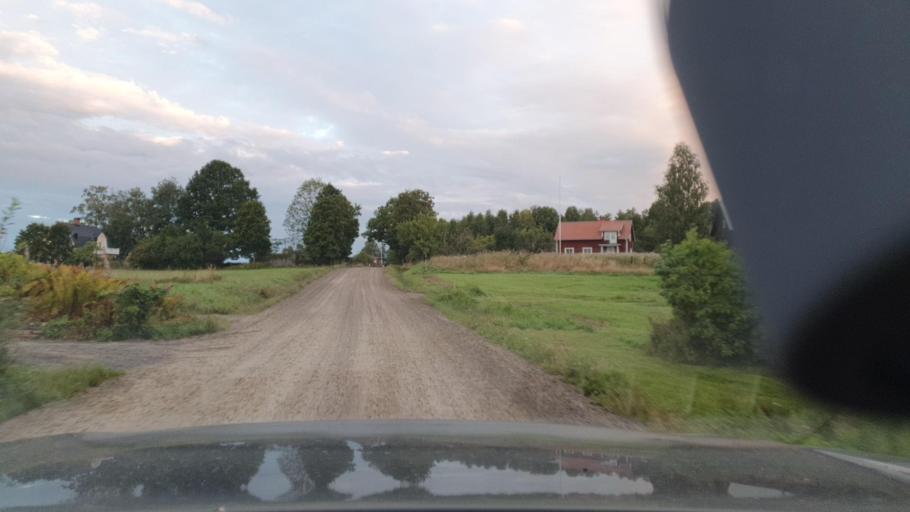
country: SE
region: Vaermland
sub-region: Sunne Kommun
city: Sunne
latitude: 59.7978
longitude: 13.1076
